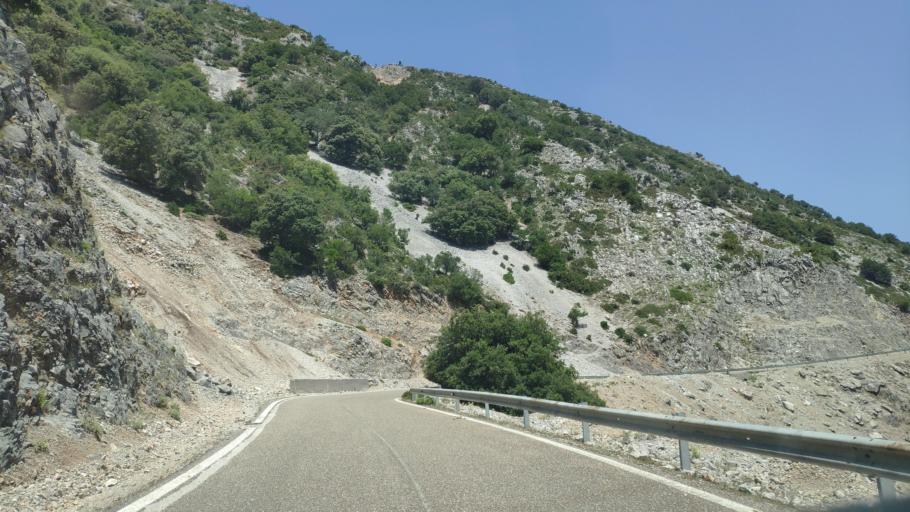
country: GR
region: West Greece
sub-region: Nomos Aitolias kai Akarnanias
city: Krikellos
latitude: 39.0180
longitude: 21.3692
